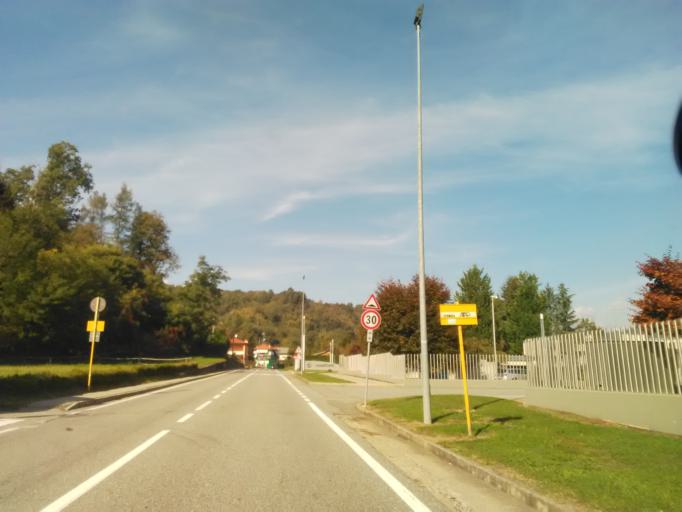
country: IT
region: Piedmont
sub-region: Provincia di Novara
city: Grignasco
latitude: 45.6601
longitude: 8.3344
